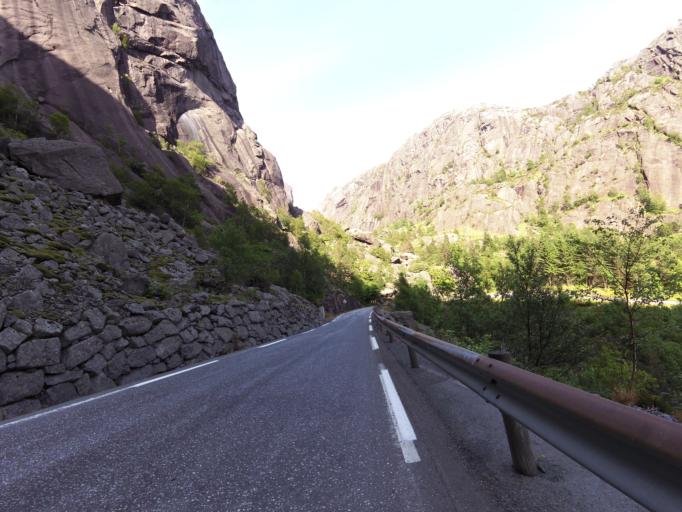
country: NO
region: Rogaland
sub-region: Sokndal
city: Hauge i Dalane
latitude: 58.3327
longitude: 6.3586
